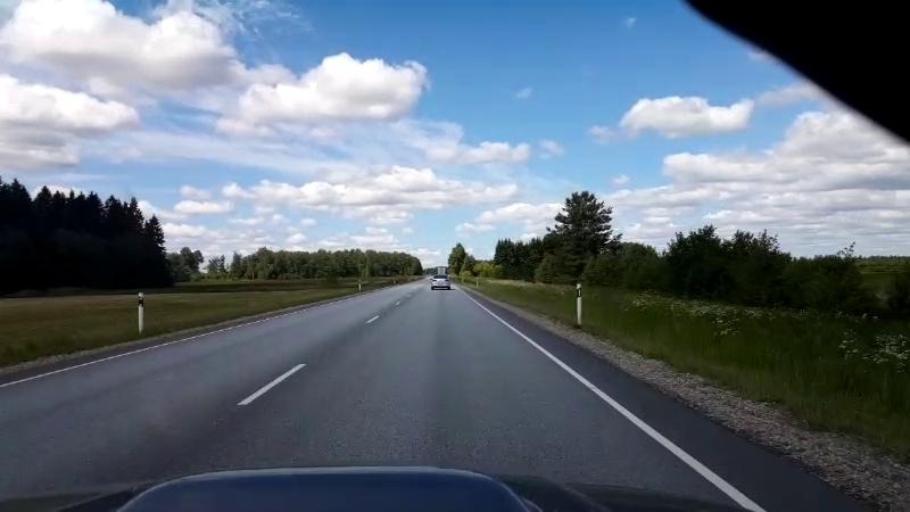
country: EE
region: Paernumaa
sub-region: Halinga vald
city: Parnu-Jaagupi
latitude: 58.5602
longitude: 24.5214
